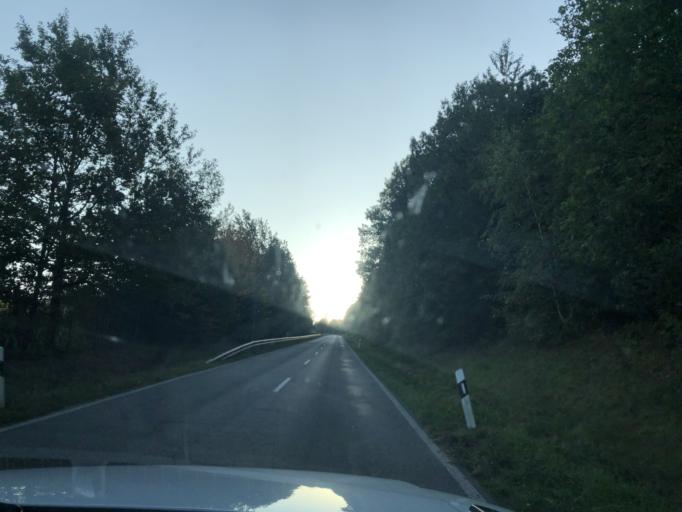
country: DE
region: Rheinland-Pfalz
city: Mertesdorf
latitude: 49.7711
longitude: 6.7398
